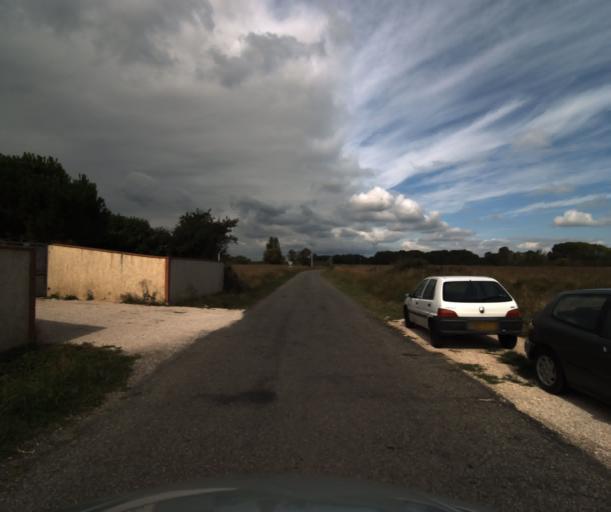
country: FR
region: Midi-Pyrenees
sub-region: Departement de la Haute-Garonne
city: Seysses
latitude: 43.4598
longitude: 1.3073
